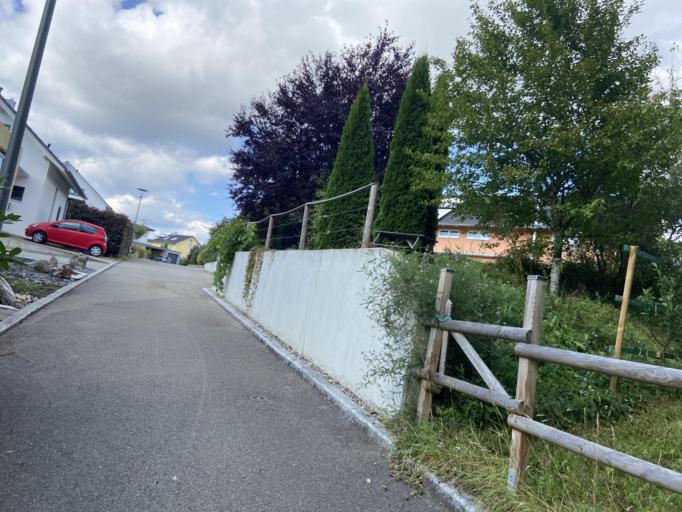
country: DE
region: Baden-Wuerttemberg
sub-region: Tuebingen Region
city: Sigmaringendorf
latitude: 48.0735
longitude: 9.2575
